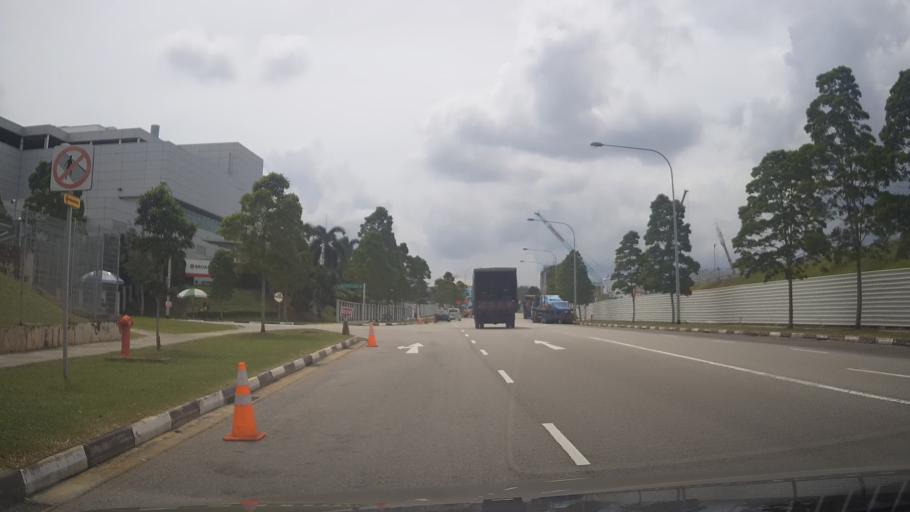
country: MY
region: Johor
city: Johor Bahru
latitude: 1.4573
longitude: 103.7946
